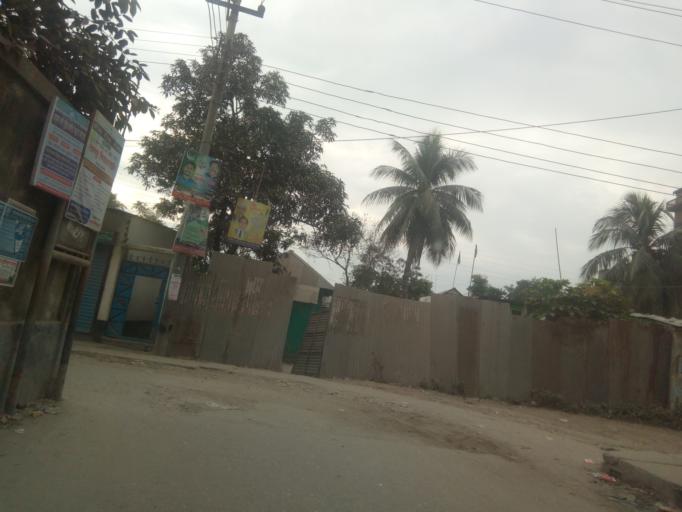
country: BD
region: Dhaka
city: Narayanganj
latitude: 23.5909
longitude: 90.5059
